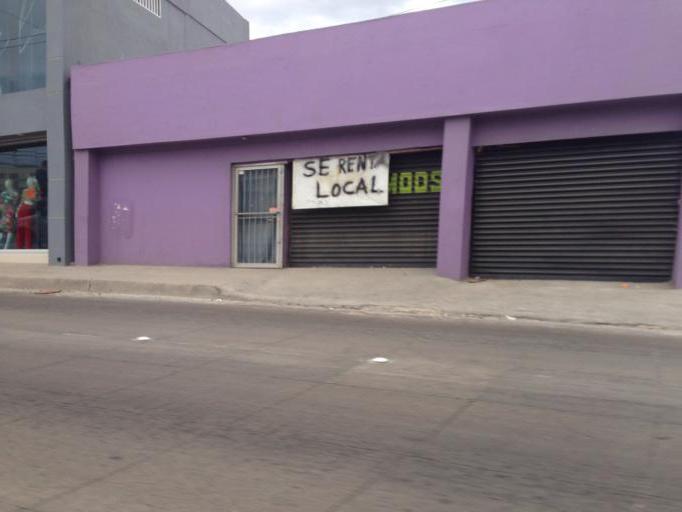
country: MX
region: Baja California
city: Tijuana
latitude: 32.5230
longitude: -117.0285
